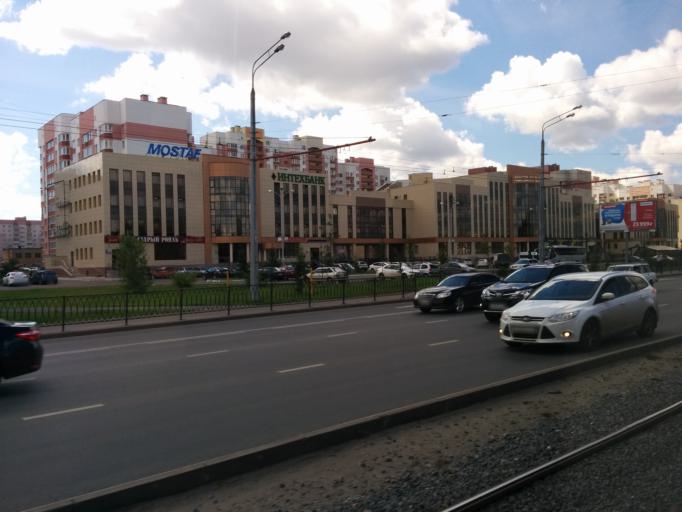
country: RU
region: Tatarstan
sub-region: Gorod Kazan'
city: Kazan
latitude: 55.8271
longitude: 49.1143
